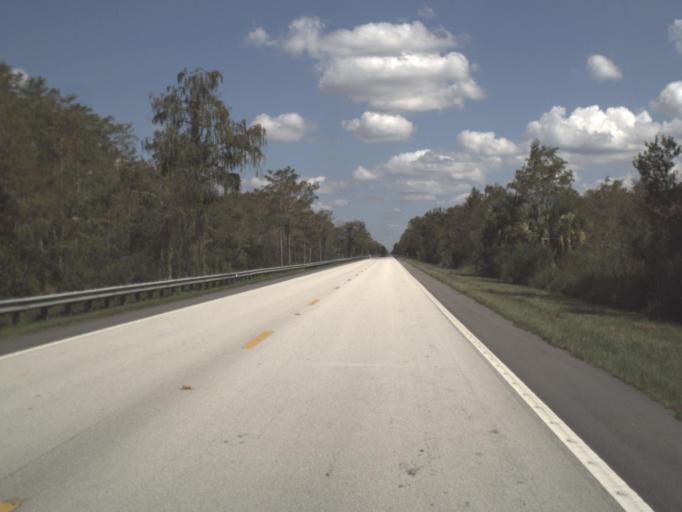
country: US
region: Florida
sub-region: Miami-Dade County
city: Kendall West
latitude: 25.8523
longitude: -80.9886
